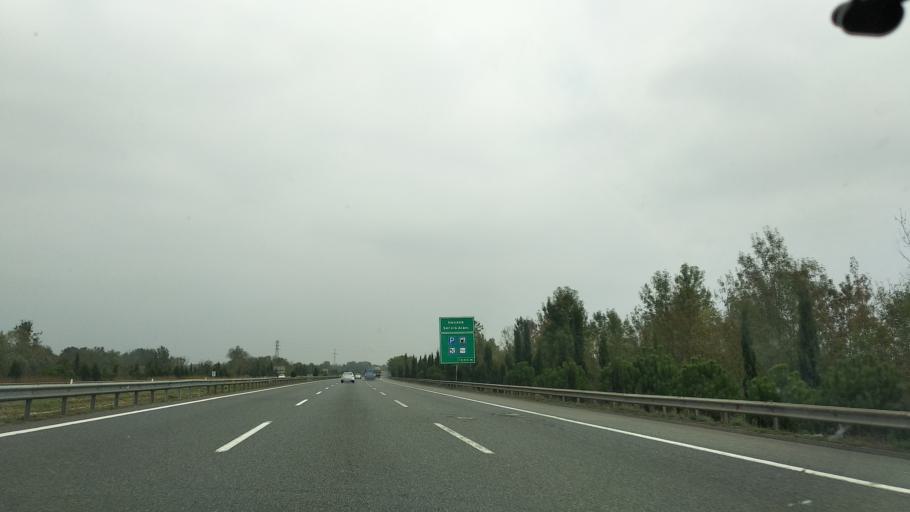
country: TR
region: Sakarya
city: Akyazi
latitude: 40.7475
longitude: 30.6799
